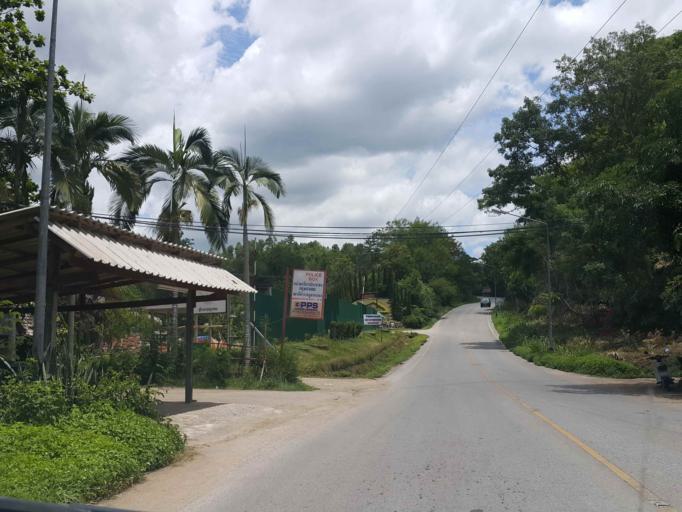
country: TH
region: Chiang Mai
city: Hang Dong
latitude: 18.7720
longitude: 98.8626
